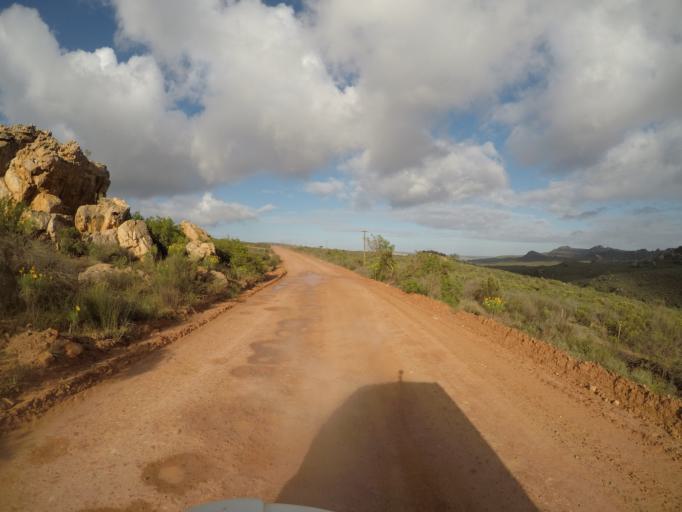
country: ZA
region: Western Cape
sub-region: West Coast District Municipality
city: Clanwilliam
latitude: -32.3414
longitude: 18.7599
